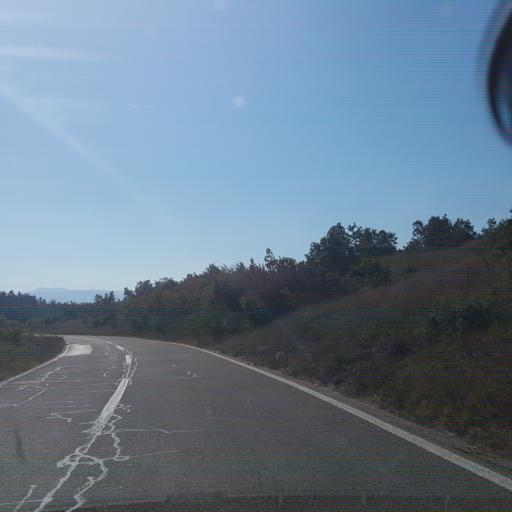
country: RS
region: Central Serbia
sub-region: Zajecarski Okrug
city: Knjazevac
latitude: 43.4674
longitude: 22.2169
